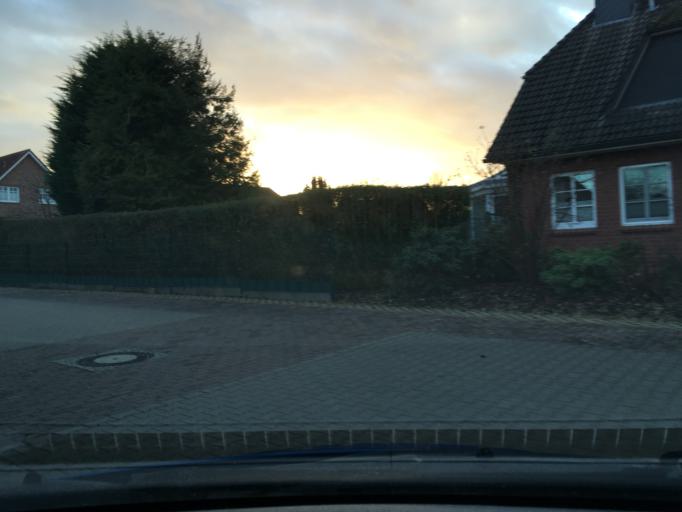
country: DE
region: Lower Saxony
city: Amelinghausen
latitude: 53.1370
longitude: 10.2153
